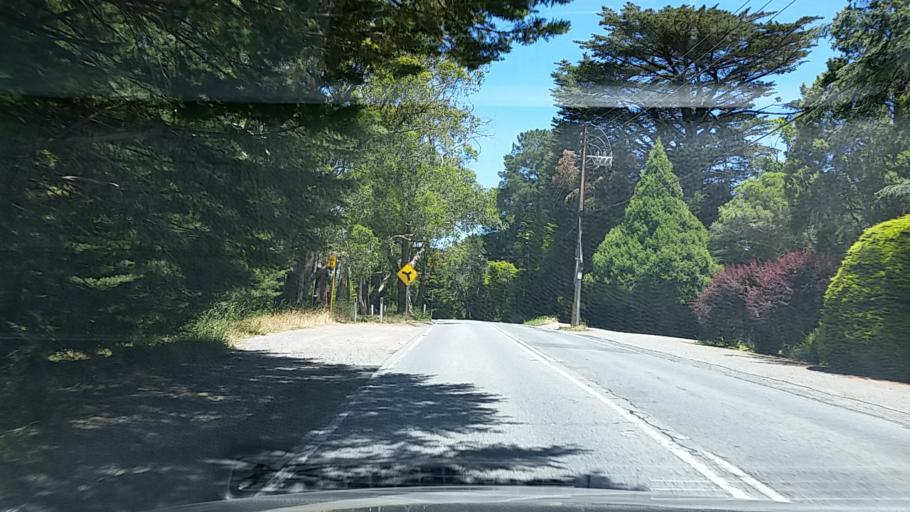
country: AU
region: South Australia
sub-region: Adelaide Hills
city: Crafers
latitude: -35.0055
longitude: 138.6993
